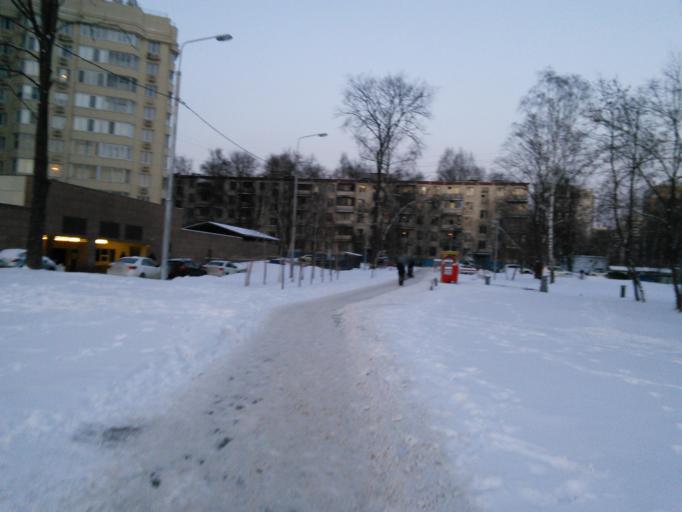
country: RU
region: Moskovskaya
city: Bol'shaya Setun'
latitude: 55.7406
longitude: 37.4185
